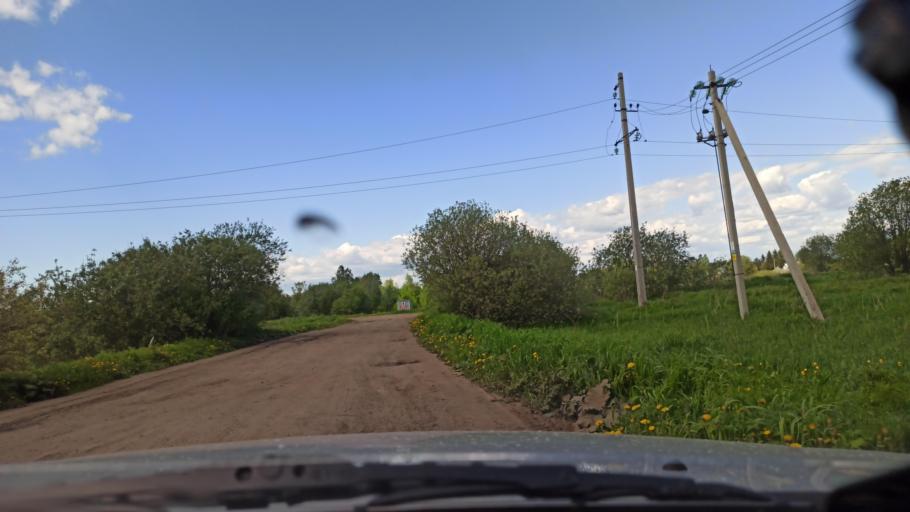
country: RU
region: Vologda
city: Vologda
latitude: 59.3402
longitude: 39.8383
